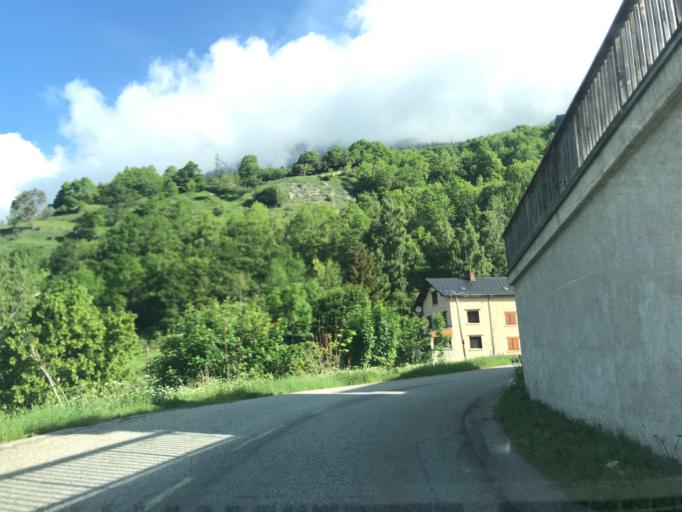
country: FR
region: Rhone-Alpes
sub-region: Departement de la Savoie
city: Modane
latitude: 45.2058
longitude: 6.6339
